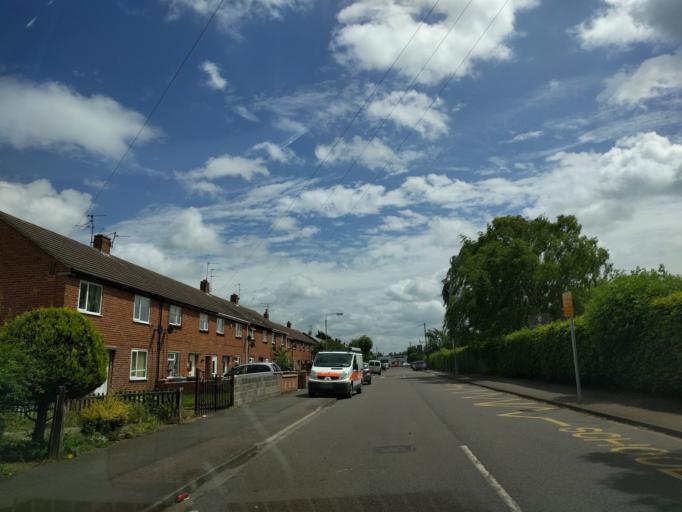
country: GB
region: England
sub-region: Nottinghamshire
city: Newark on Trent
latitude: 53.0611
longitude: -0.8080
